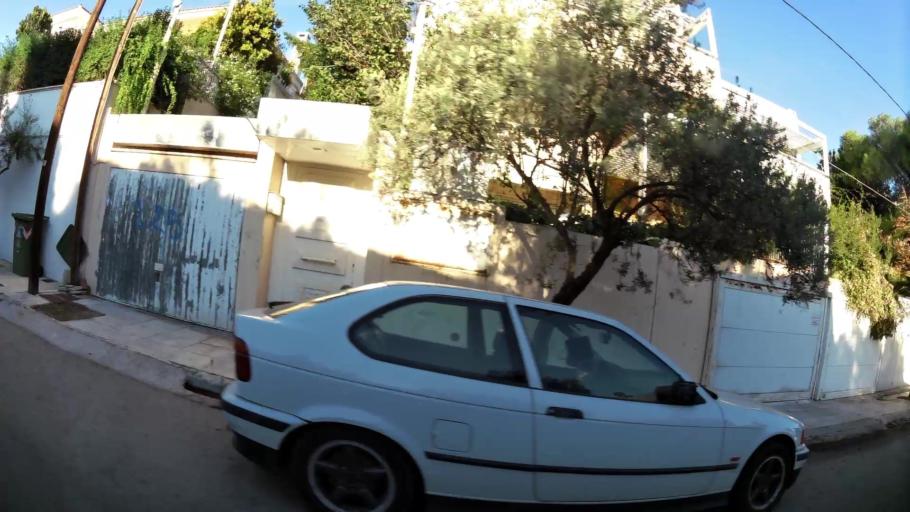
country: GR
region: Attica
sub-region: Nomarchia Athinas
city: Nea Erythraia
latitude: 38.0878
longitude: 23.8282
